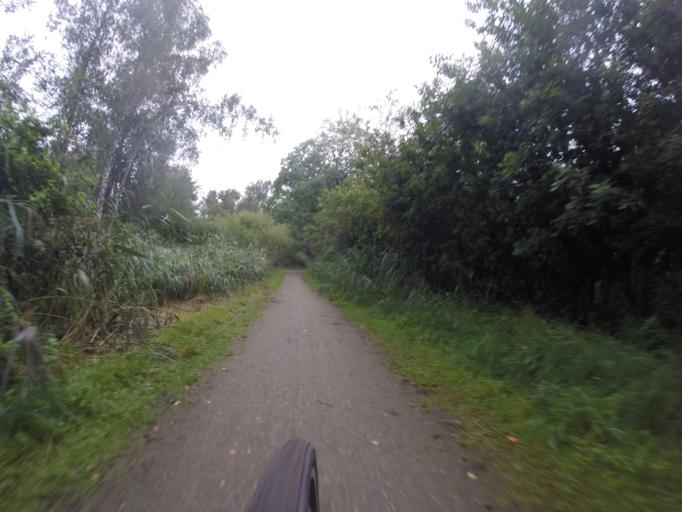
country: DK
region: Capital Region
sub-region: Herlev Kommune
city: Herlev
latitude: 55.7550
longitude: 12.4318
